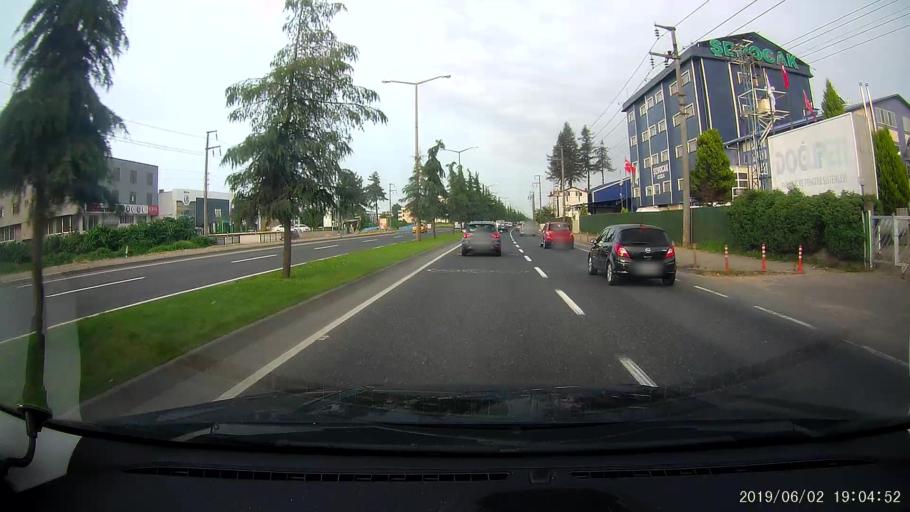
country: TR
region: Ordu
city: Ordu
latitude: 40.9774
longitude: 37.9456
